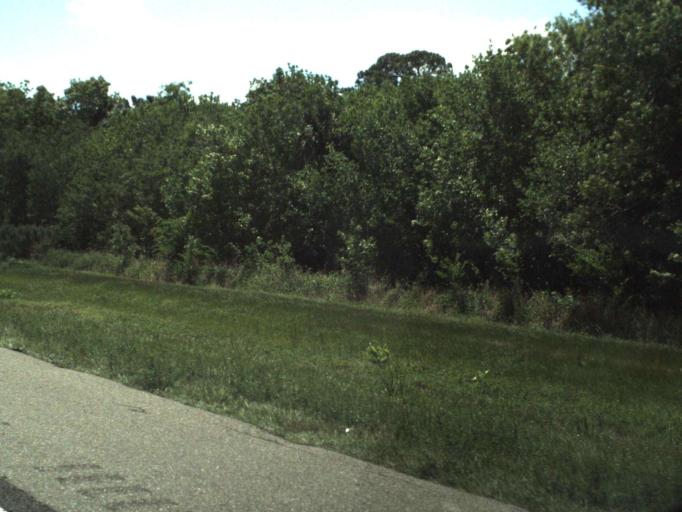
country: US
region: Florida
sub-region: Volusia County
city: DeBary
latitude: 28.8487
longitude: -81.3062
